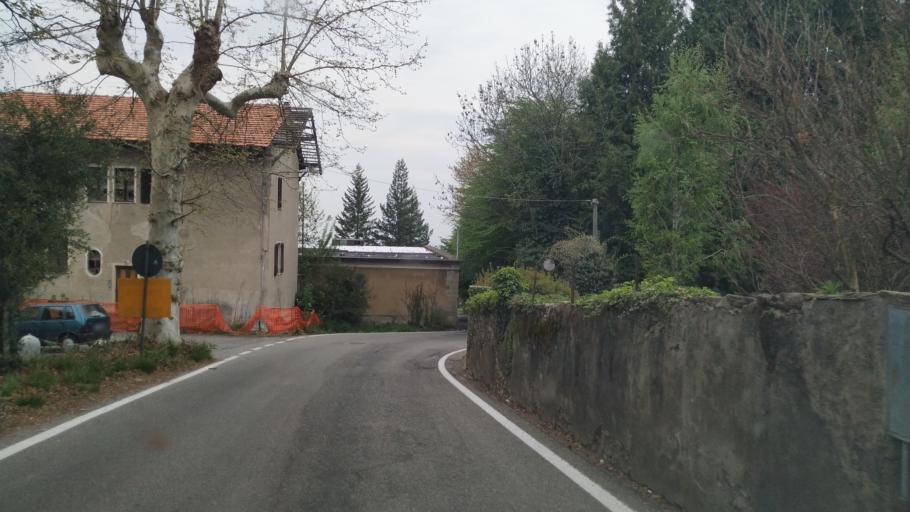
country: IT
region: Piedmont
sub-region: Provincia di Biella
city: Pollone
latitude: 45.5844
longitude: 8.0044
